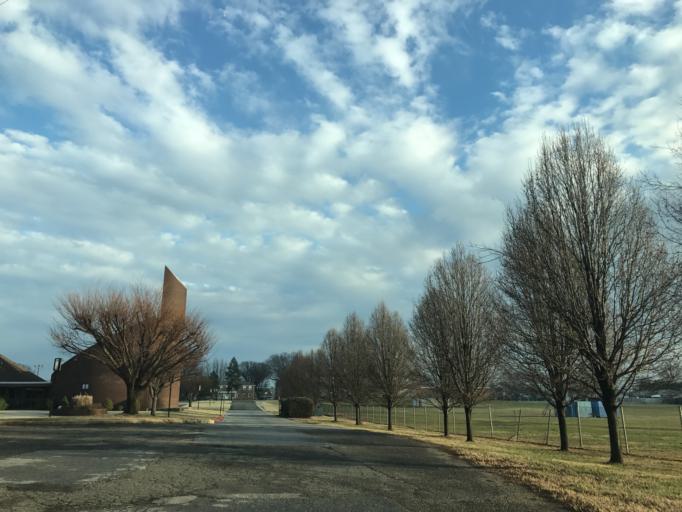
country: US
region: Maryland
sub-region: Baltimore County
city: Dundalk
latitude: 39.2691
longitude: -76.4944
